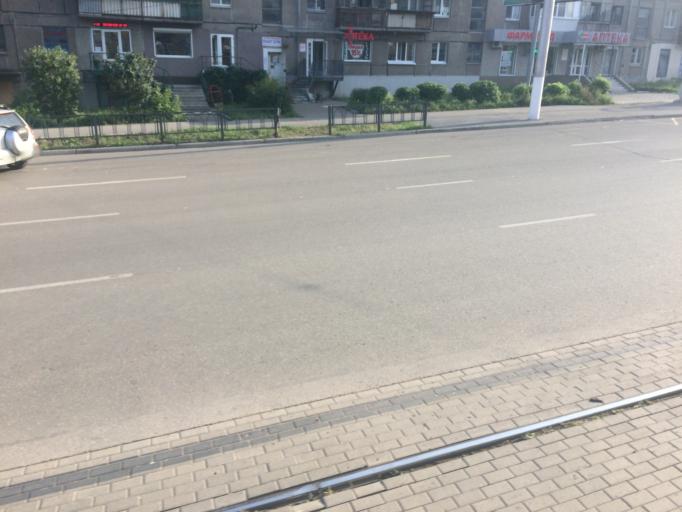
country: RU
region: Chelyabinsk
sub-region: Gorod Magnitogorsk
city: Magnitogorsk
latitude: 53.3980
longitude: 58.9809
